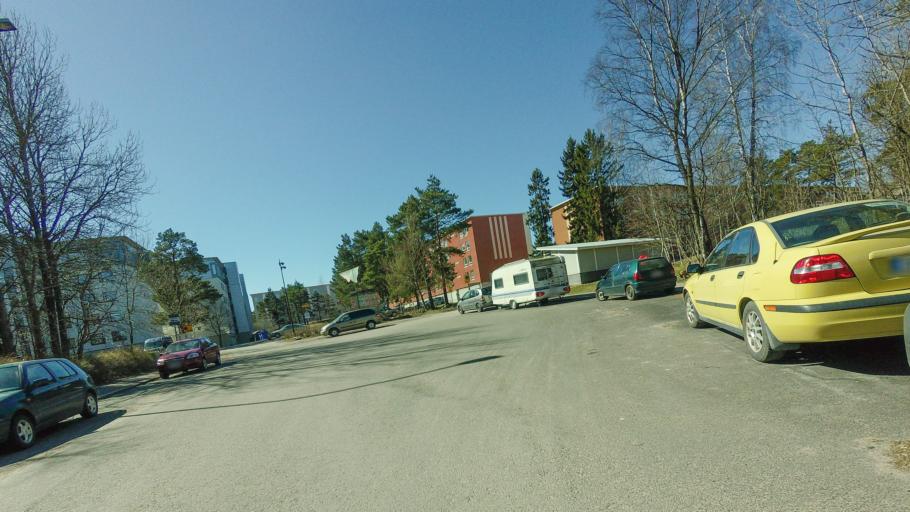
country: FI
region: Uusimaa
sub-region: Helsinki
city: Helsinki
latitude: 60.1667
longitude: 25.0464
